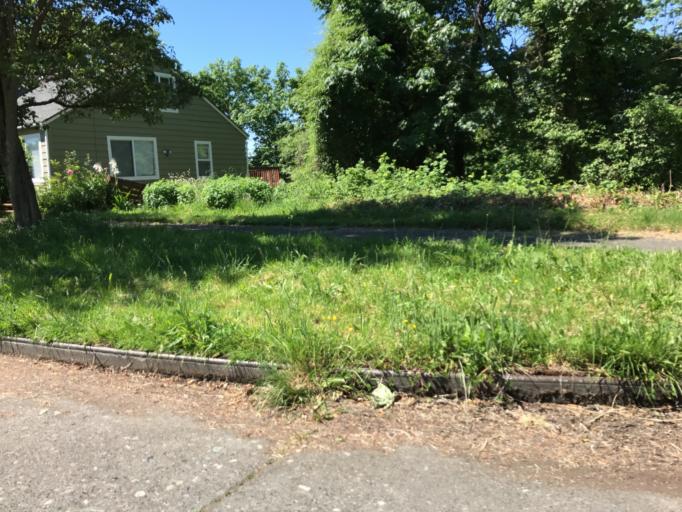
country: US
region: Washington
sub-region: King County
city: Seattle
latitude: 47.5869
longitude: -122.2956
